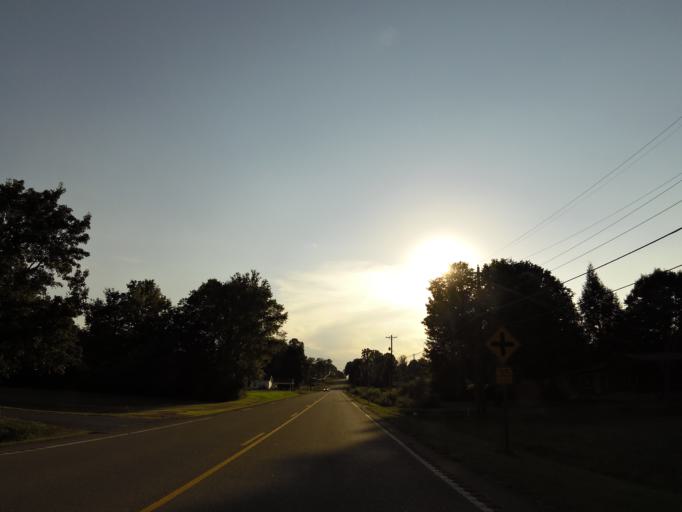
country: US
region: Tennessee
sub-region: McMinn County
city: Englewood
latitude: 35.4255
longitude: -84.5314
